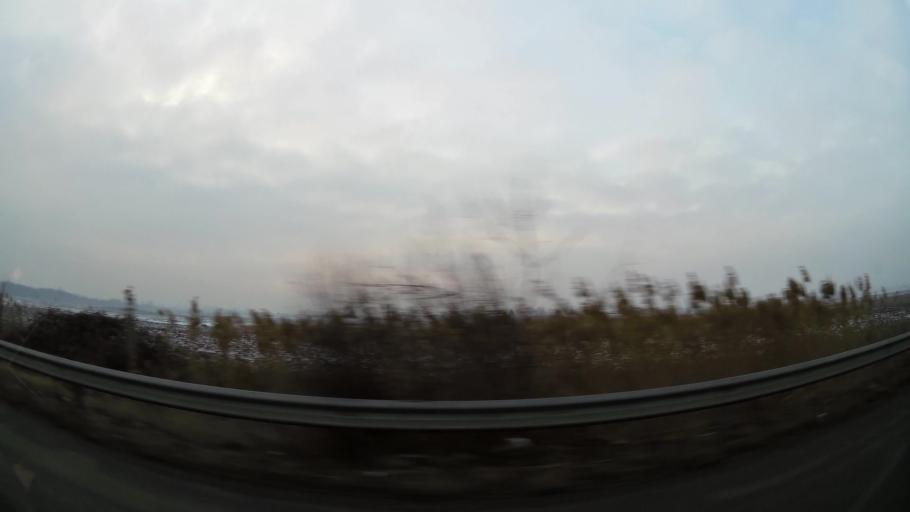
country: MK
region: Aracinovo
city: Arachinovo
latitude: 42.0002
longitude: 21.5332
